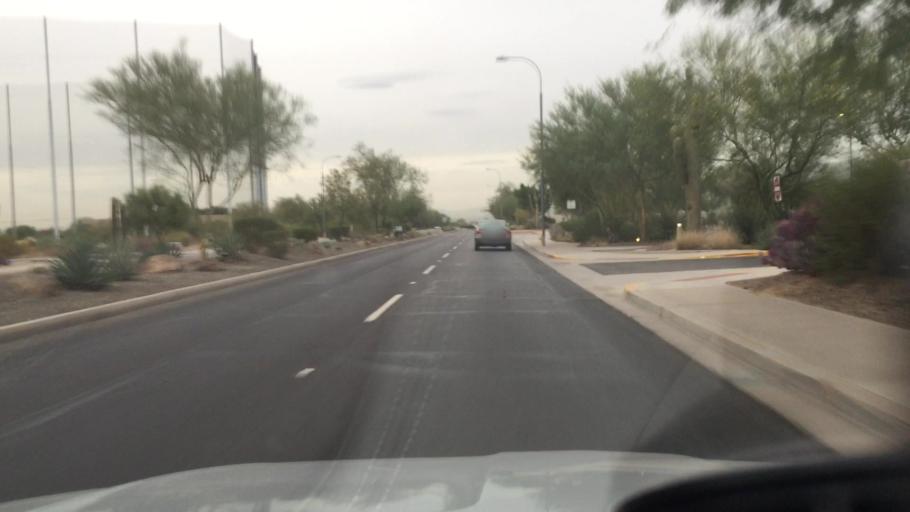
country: US
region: Arizona
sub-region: Maricopa County
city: Scottsdale
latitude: 33.5395
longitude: -111.8740
